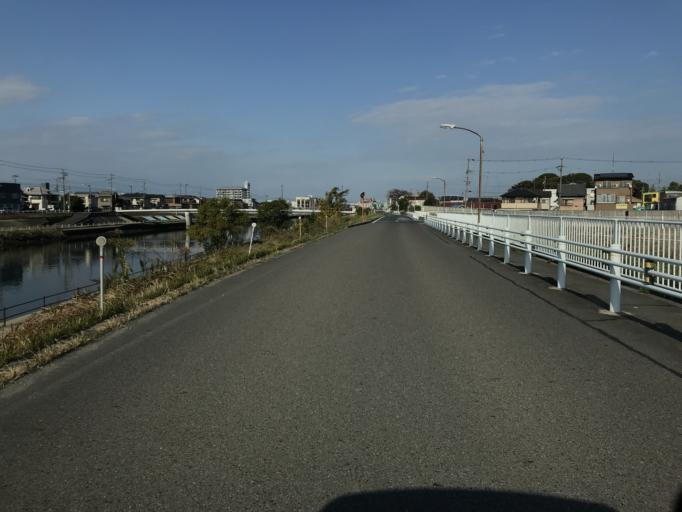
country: JP
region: Aichi
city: Nagoya-shi
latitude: 35.1901
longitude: 136.8489
